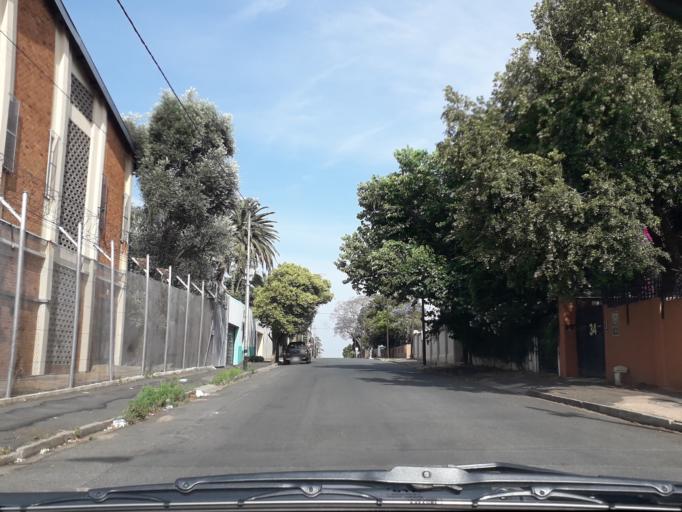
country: ZA
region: Gauteng
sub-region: City of Johannesburg Metropolitan Municipality
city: Johannesburg
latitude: -26.1576
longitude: 28.0881
